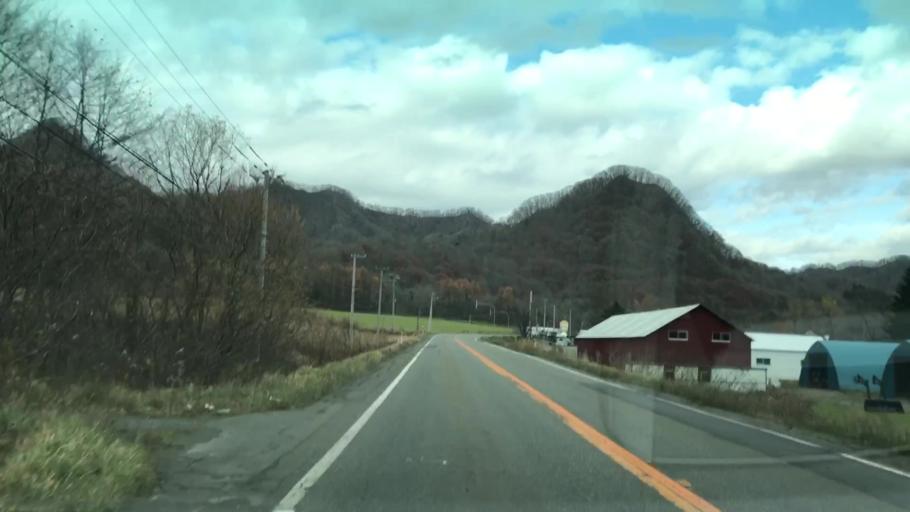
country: JP
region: Hokkaido
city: Shizunai-furukawacho
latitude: 42.8025
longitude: 142.3978
